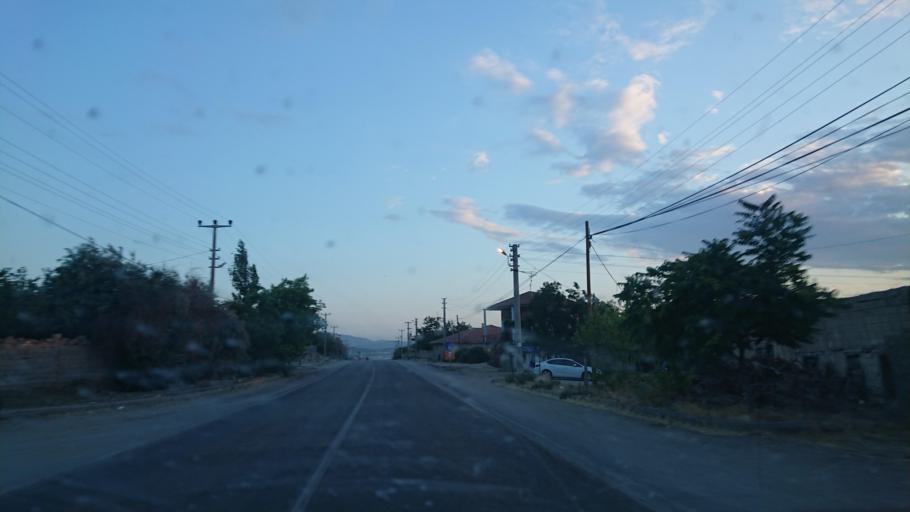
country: TR
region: Aksaray
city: Balci
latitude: 38.7899
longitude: 34.1222
